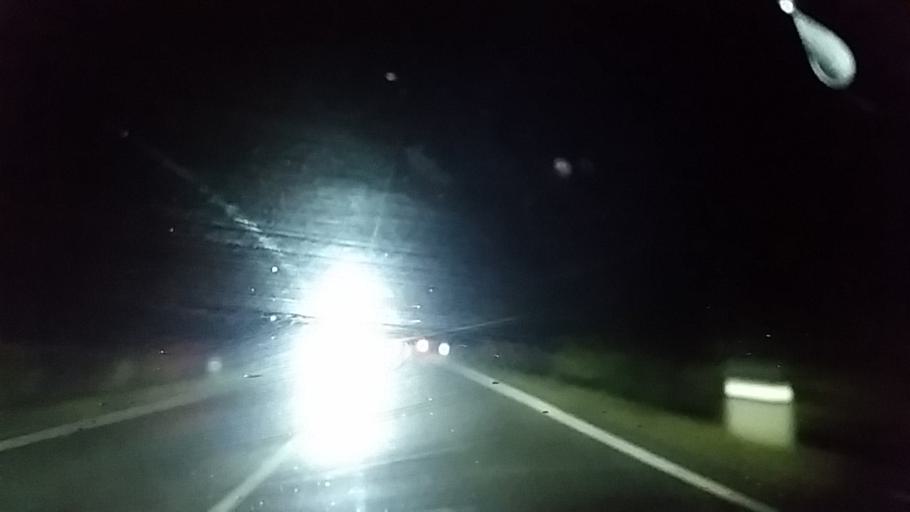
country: DE
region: Lower Saxony
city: Marschacht
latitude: 53.3973
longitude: 10.3324
